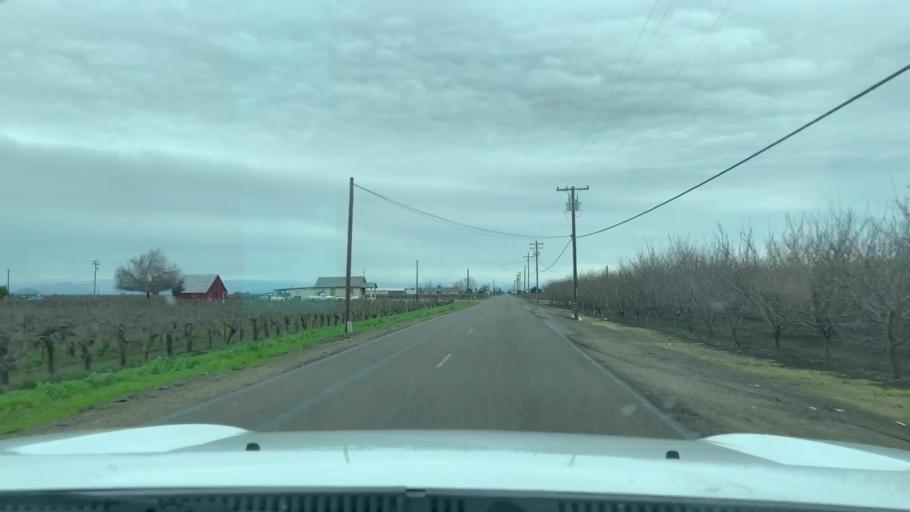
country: US
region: California
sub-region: Fresno County
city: Fowler
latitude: 36.5473
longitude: -119.7251
